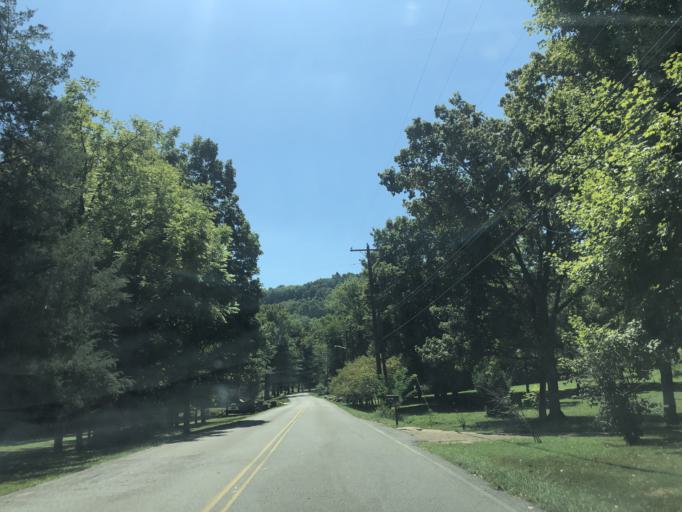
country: US
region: Tennessee
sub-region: Davidson County
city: Oak Hill
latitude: 36.0797
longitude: -86.7919
